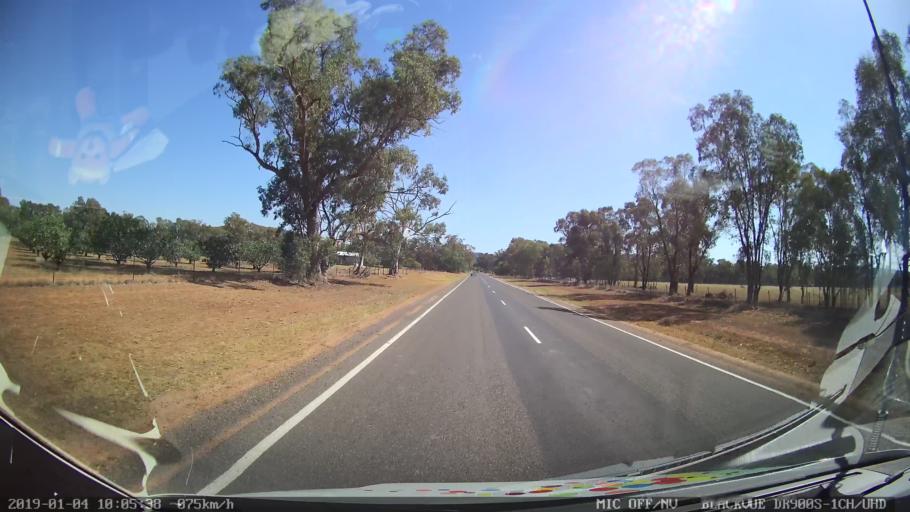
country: AU
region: New South Wales
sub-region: Cabonne
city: Canowindra
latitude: -33.4395
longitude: 148.3659
